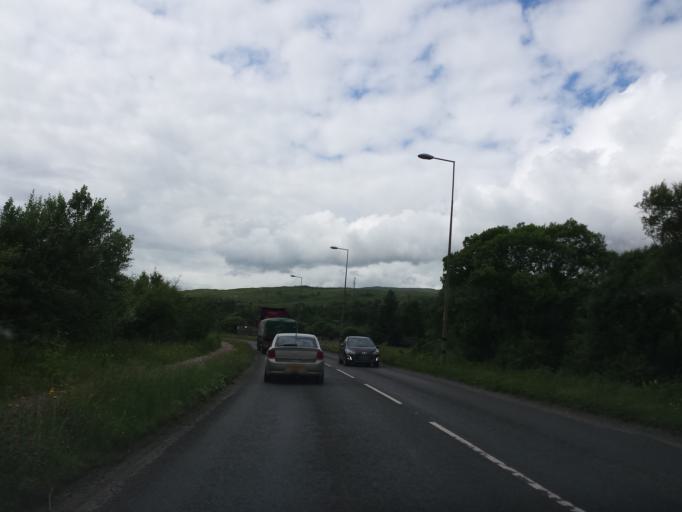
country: GB
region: Scotland
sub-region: Highland
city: Fort William
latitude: 56.8426
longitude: -5.0892
